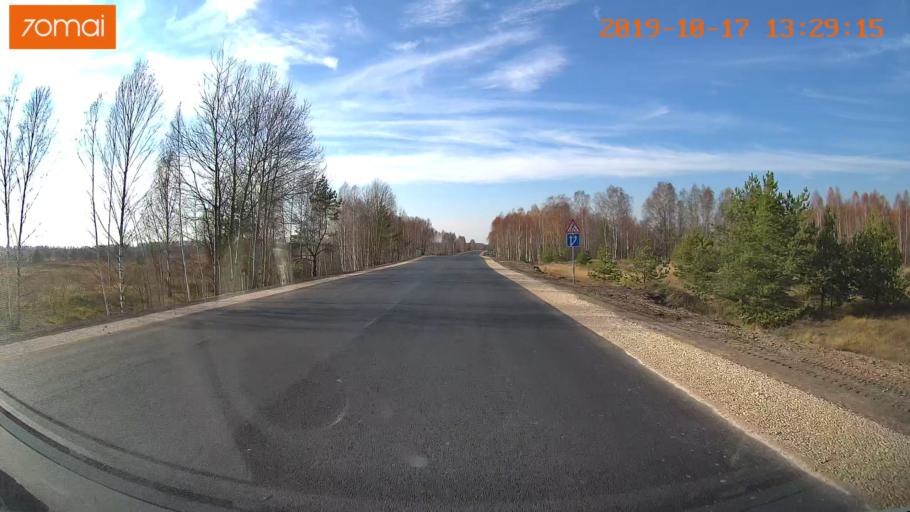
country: RU
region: Vladimir
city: Velikodvorskiy
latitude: 55.1188
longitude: 40.8459
